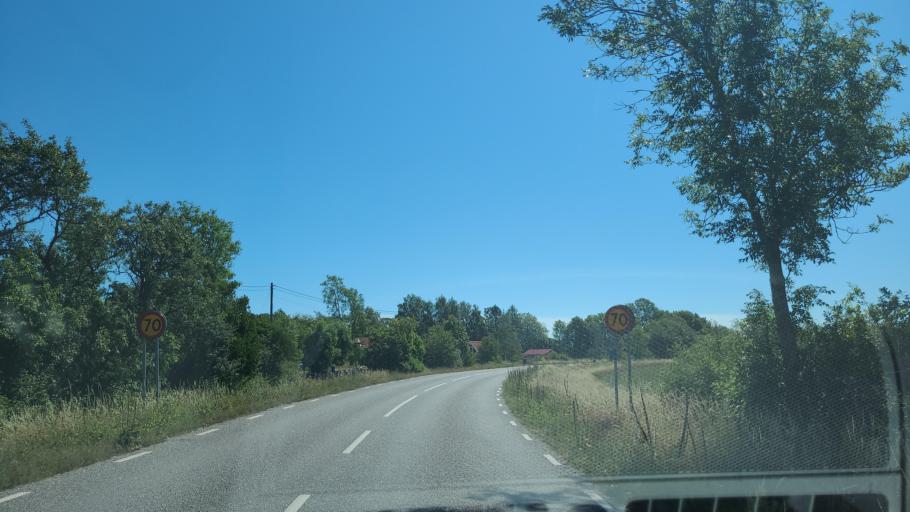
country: SE
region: Kalmar
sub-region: Borgholms Kommun
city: Borgholm
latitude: 56.7717
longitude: 16.5822
